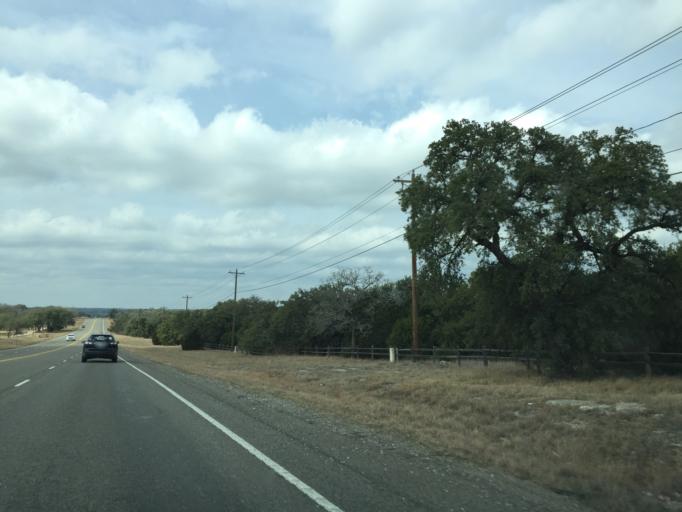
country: US
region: Texas
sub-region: Burnet County
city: Marble Falls
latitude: 30.4900
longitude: -98.2229
